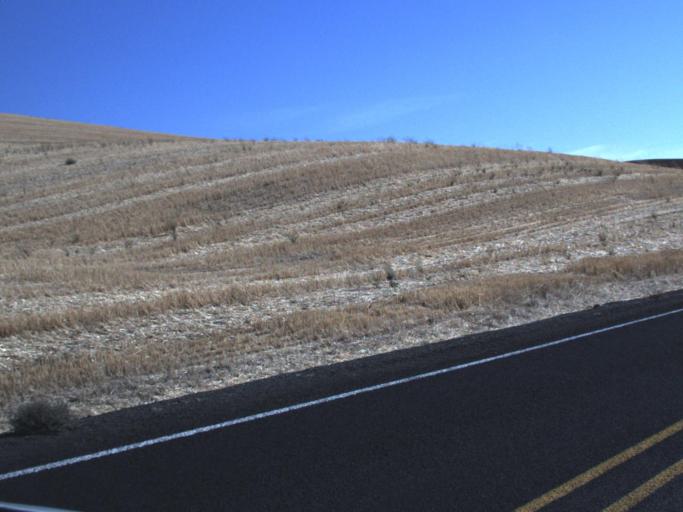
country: US
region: Washington
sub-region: Walla Walla County
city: Walla Walla
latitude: 46.1974
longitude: -118.3815
